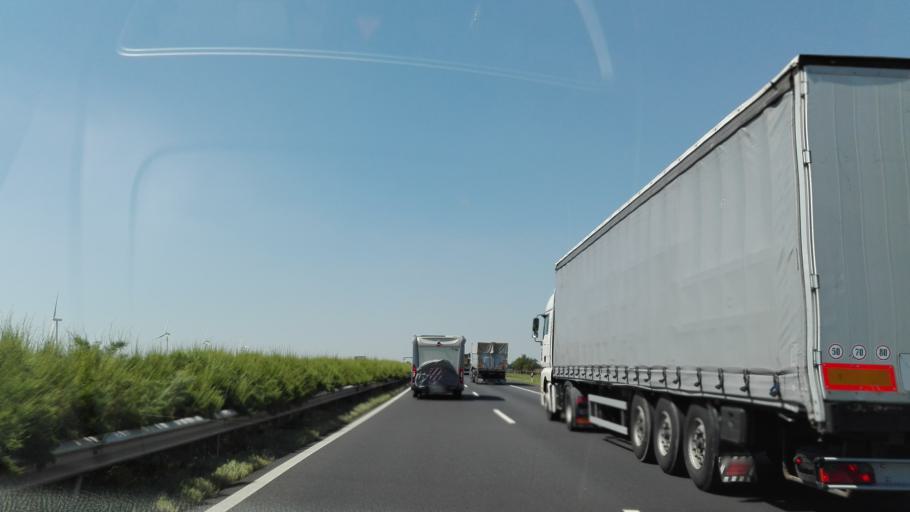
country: HU
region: Gyor-Moson-Sopron
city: Mosonmagyarovar
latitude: 47.8762
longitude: 17.2068
